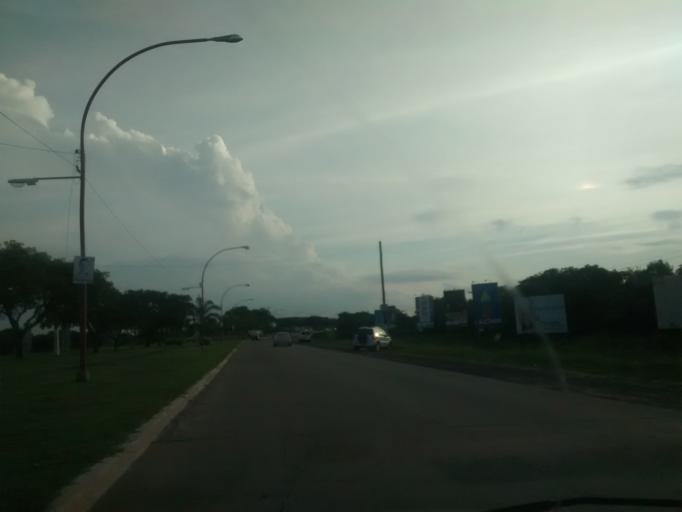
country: AR
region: Chaco
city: Resistencia
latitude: -27.4257
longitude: -58.9599
